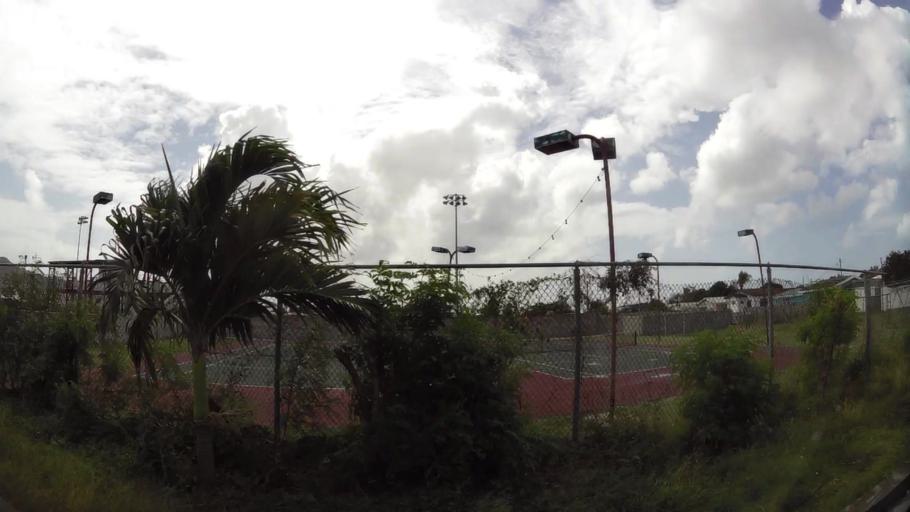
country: KN
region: Saint George Basseterre
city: Basseterre
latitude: 17.2982
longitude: -62.7169
